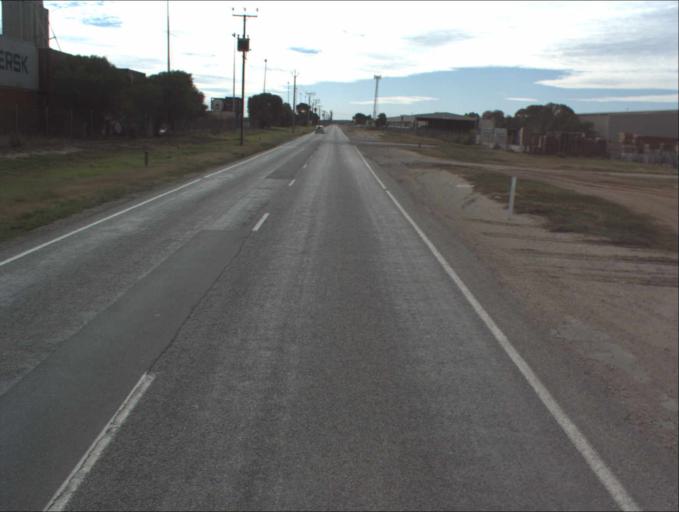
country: AU
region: South Australia
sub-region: Port Adelaide Enfield
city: Birkenhead
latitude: -34.8310
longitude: 138.5175
